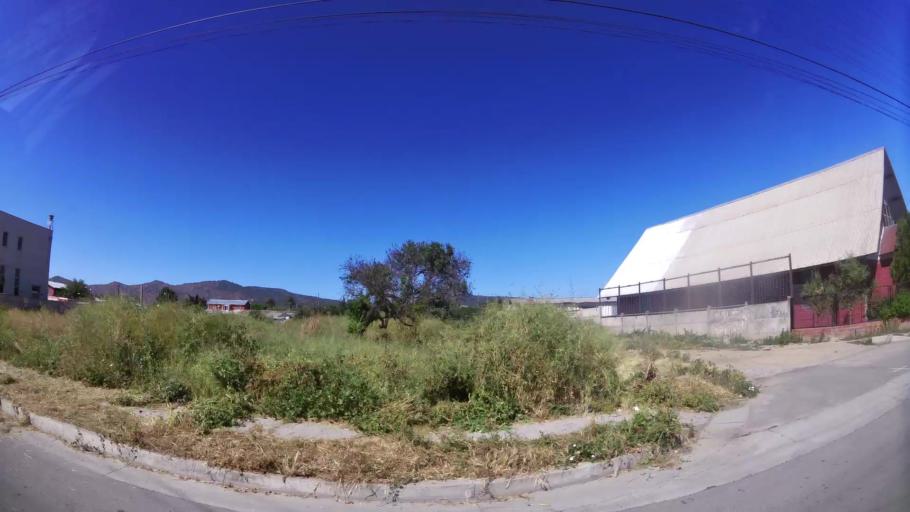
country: CL
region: Valparaiso
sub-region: Provincia de Marga Marga
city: Quilpue
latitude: -33.3167
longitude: -71.4073
